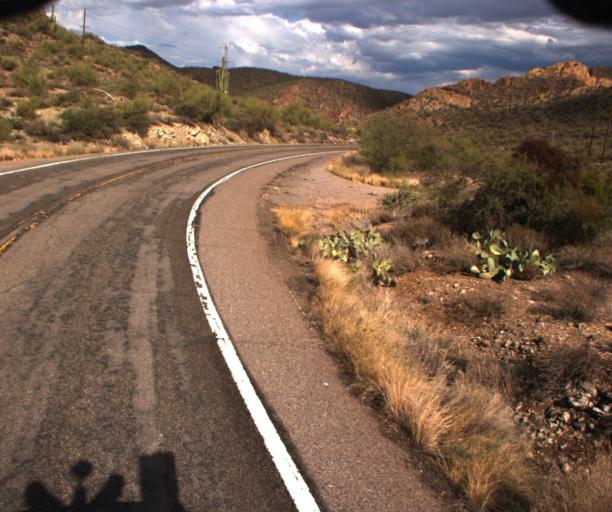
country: US
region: Arizona
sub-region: Pinal County
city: Apache Junction
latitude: 33.5128
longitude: -111.4566
